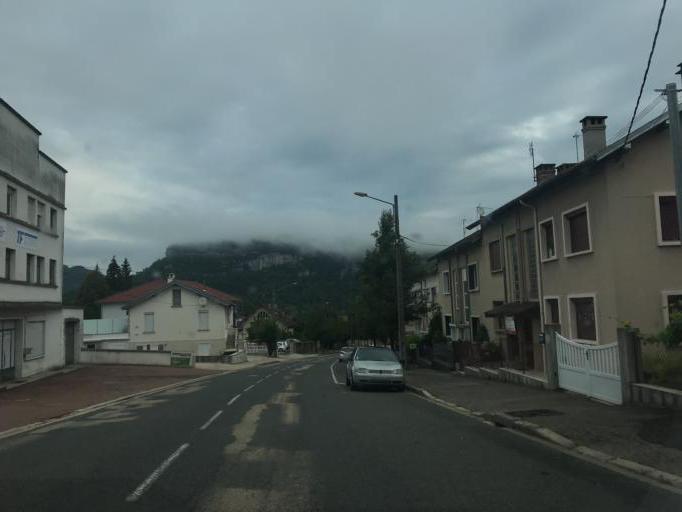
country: FR
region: Rhone-Alpes
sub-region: Departement de l'Ain
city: Dortan
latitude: 46.3155
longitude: 5.6585
